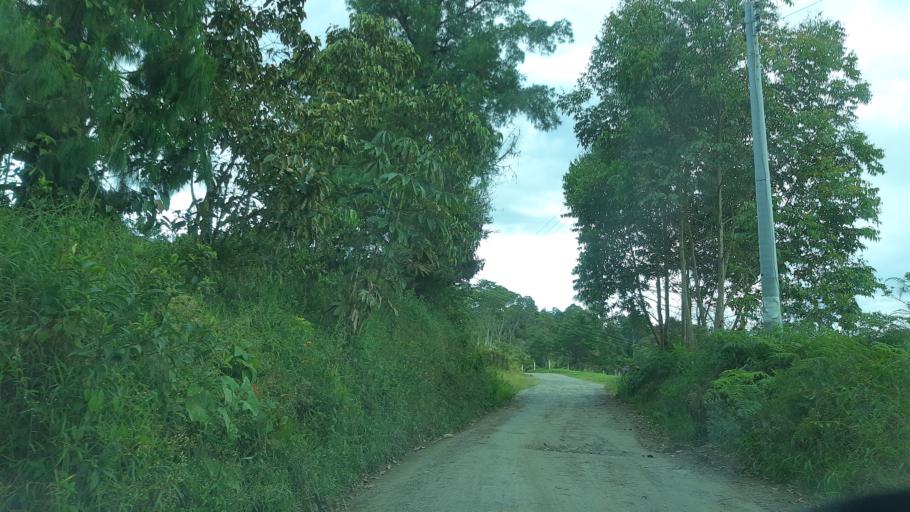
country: CO
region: Boyaca
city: Garagoa
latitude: 4.9949
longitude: -73.3286
